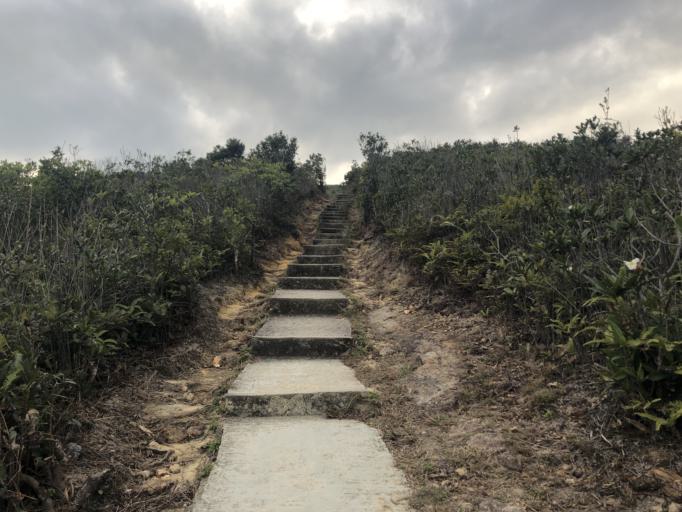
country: HK
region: Wanchai
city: Wan Chai
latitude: 22.2663
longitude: 114.2005
